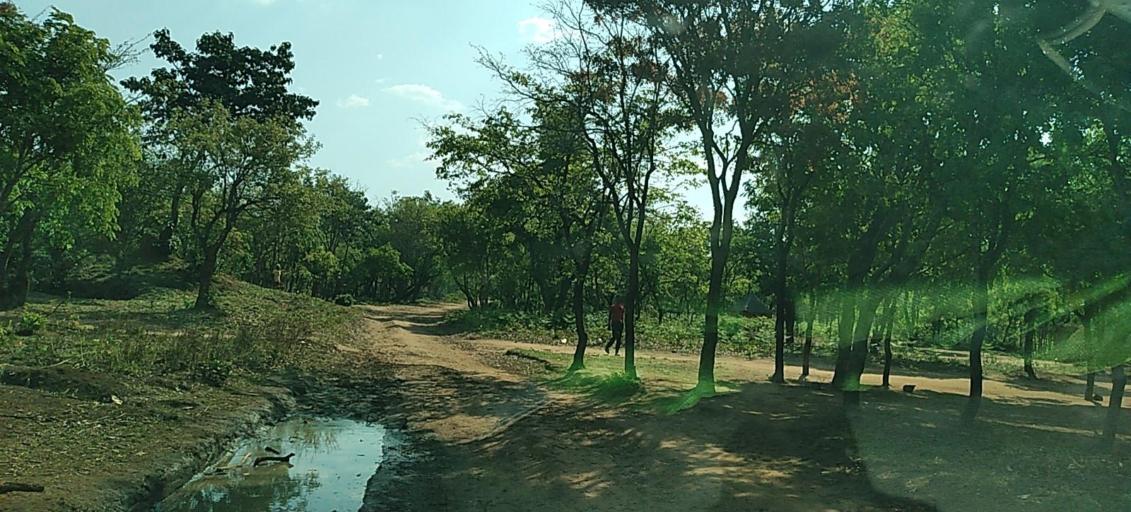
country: ZM
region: North-Western
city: Mwinilunga
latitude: -11.2995
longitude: 24.8523
